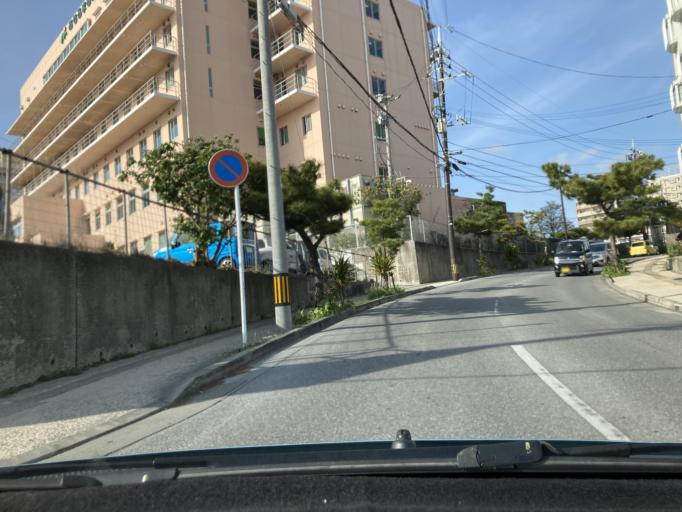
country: JP
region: Okinawa
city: Naha-shi
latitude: 26.2267
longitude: 127.6889
